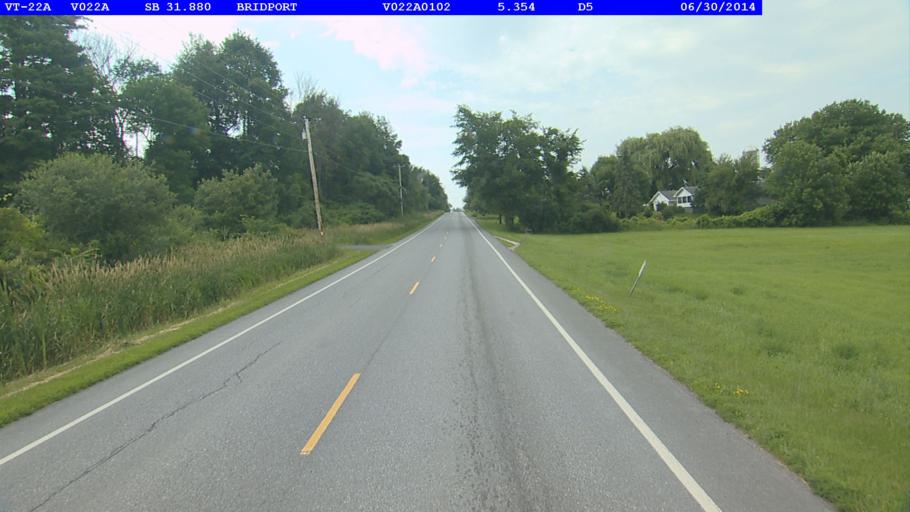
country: US
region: Vermont
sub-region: Addison County
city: Middlebury (village)
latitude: 44.0168
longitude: -73.3105
